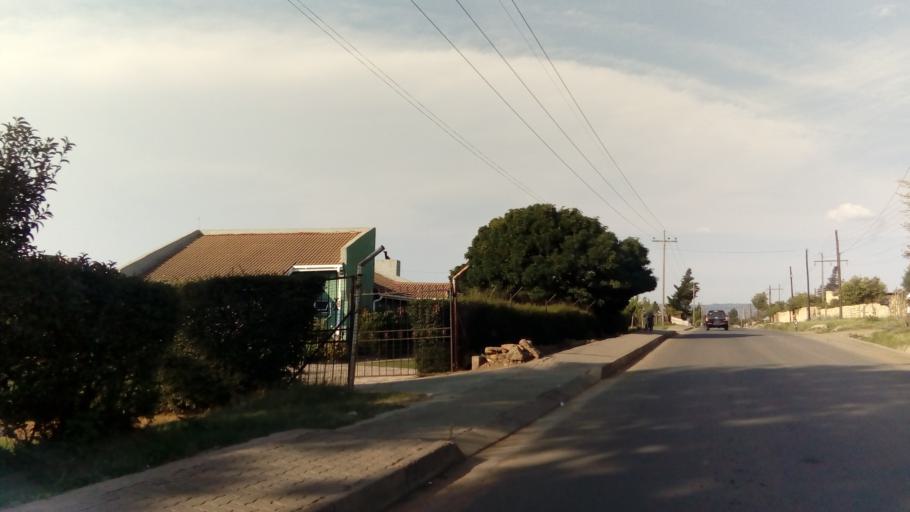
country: LS
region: Maseru
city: Maseru
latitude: -29.2879
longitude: 27.5323
